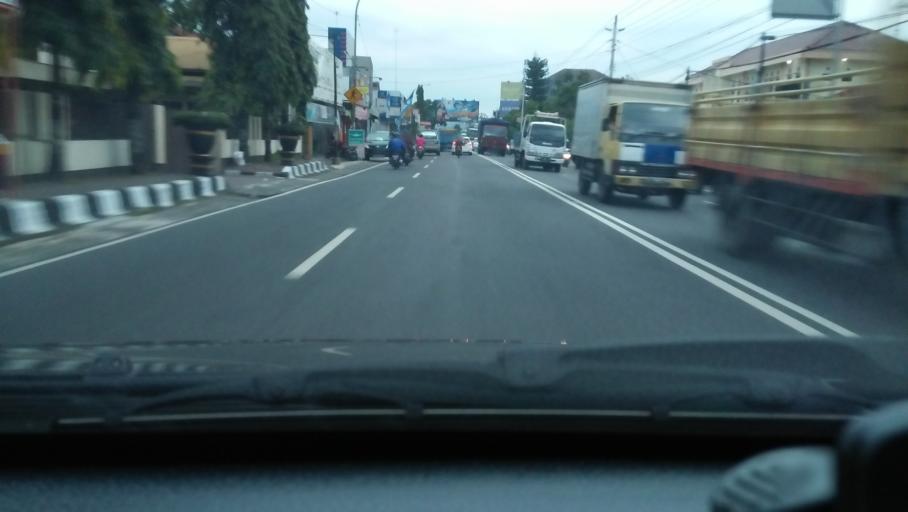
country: ID
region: Central Java
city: Magelang
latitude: -7.4543
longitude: 110.2233
